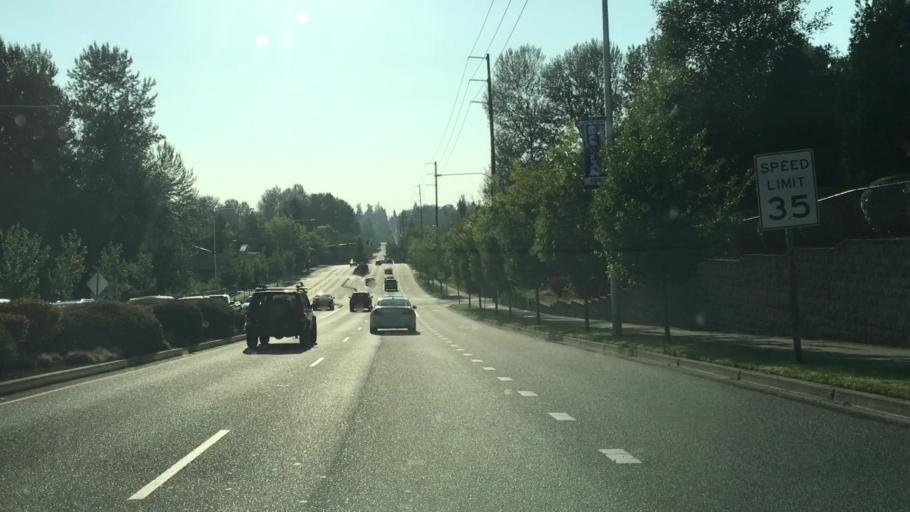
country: US
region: Washington
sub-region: King County
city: Federal Way
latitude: 47.2899
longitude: -122.3190
